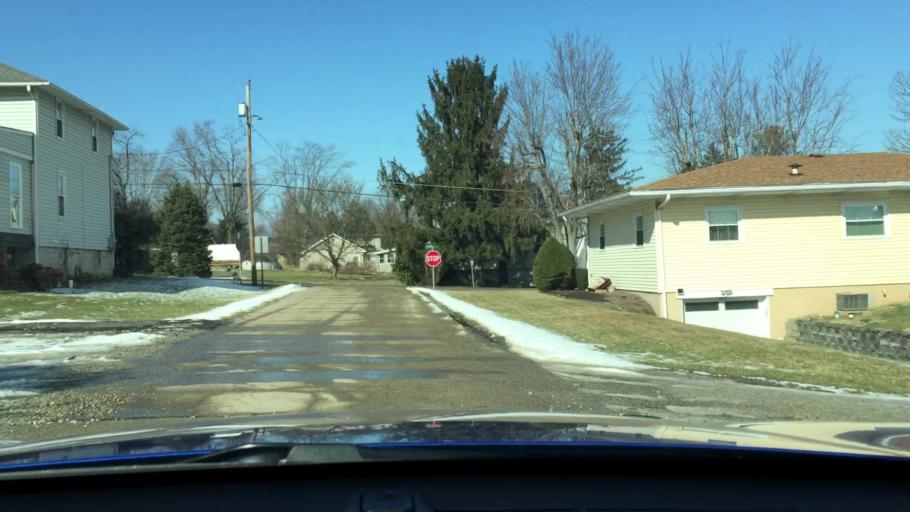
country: US
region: Pennsylvania
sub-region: Westmoreland County
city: Lynnwood-Pricedale
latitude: 40.1275
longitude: -79.8478
